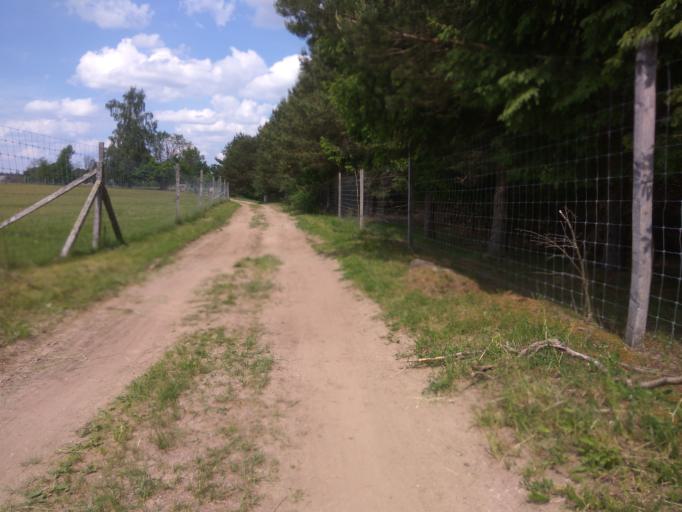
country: LV
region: Kuldigas Rajons
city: Kuldiga
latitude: 56.8879
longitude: 21.9300
